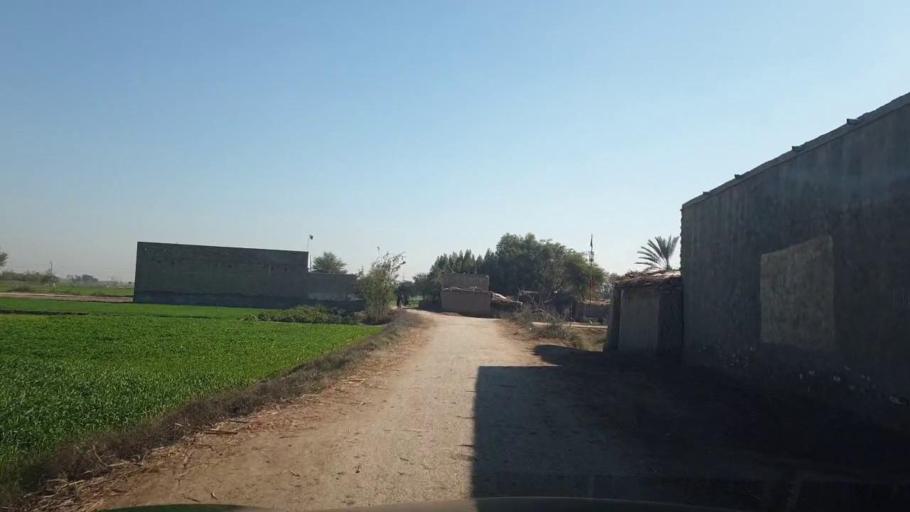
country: PK
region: Sindh
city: Ghotki
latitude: 27.9999
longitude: 69.3586
